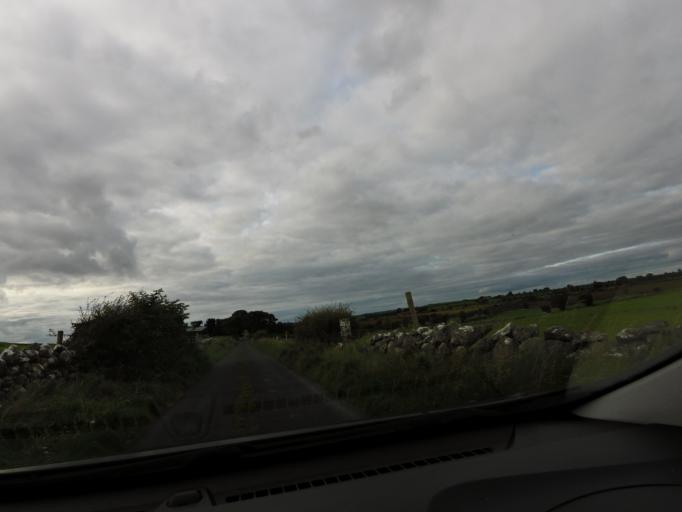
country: IE
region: Connaught
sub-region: County Galway
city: Ballinasloe
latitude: 53.3722
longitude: -8.1654
